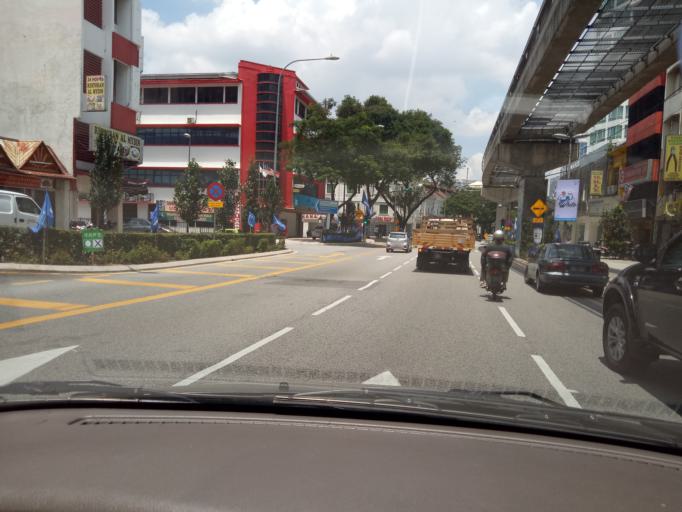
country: MY
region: Kuala Lumpur
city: Kuala Lumpur
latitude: 3.1634
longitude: 101.6980
